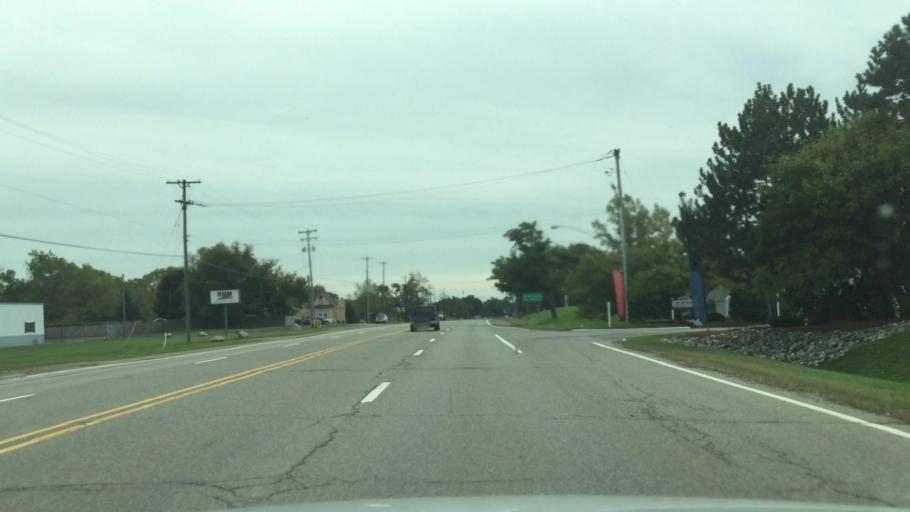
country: US
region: Michigan
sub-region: Oakland County
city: Ortonville
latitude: 42.7904
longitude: -83.5115
